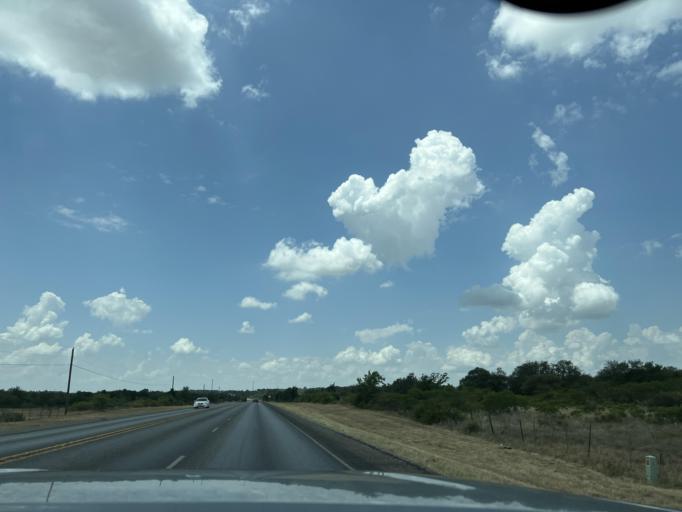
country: US
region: Texas
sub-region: Parker County
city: Springtown
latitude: 32.9309
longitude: -97.7034
